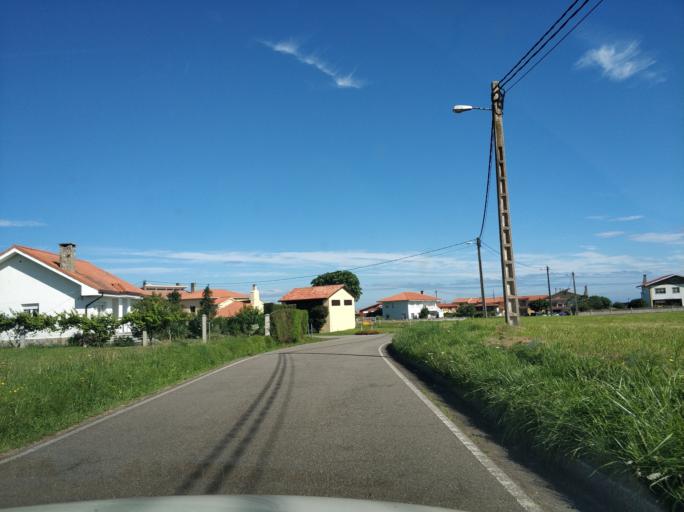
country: ES
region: Asturias
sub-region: Province of Asturias
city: Cudillero
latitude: 43.5809
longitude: -6.2408
